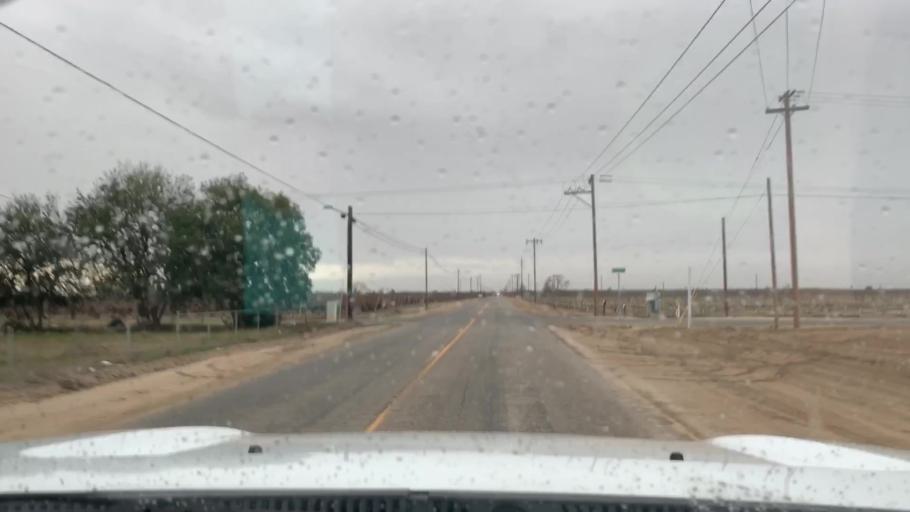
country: US
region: California
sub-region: Kern County
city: Shafter
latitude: 35.5296
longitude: -119.2779
